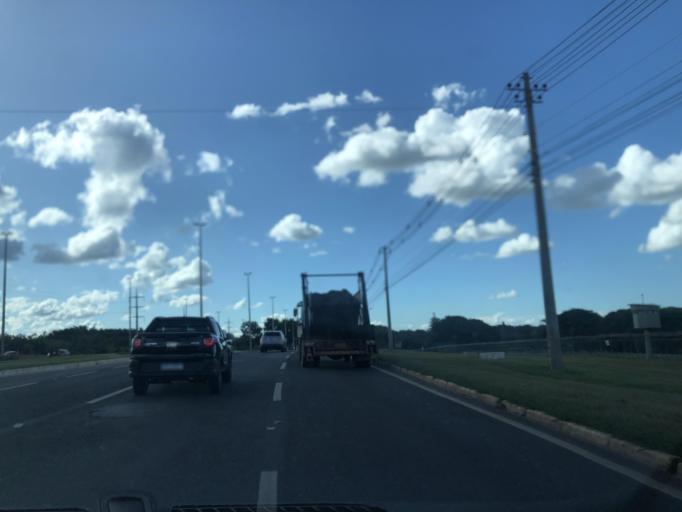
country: BR
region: Federal District
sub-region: Brasilia
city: Brasilia
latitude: -15.7834
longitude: -47.8602
